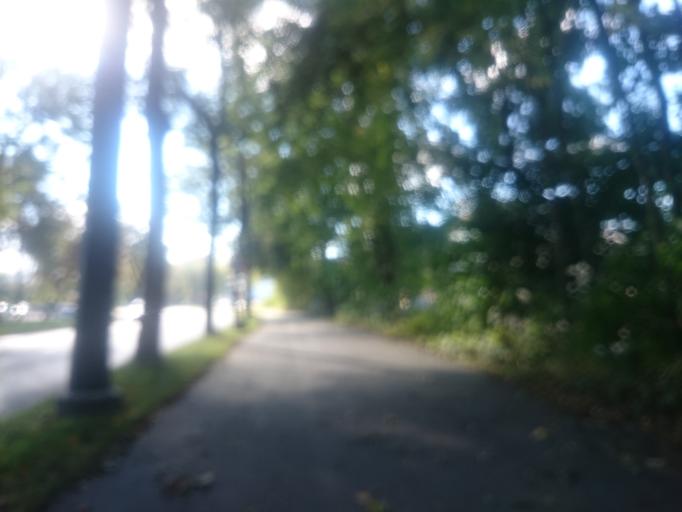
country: DE
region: Bavaria
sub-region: Swabia
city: Augsburg
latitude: 48.3688
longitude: 10.9250
